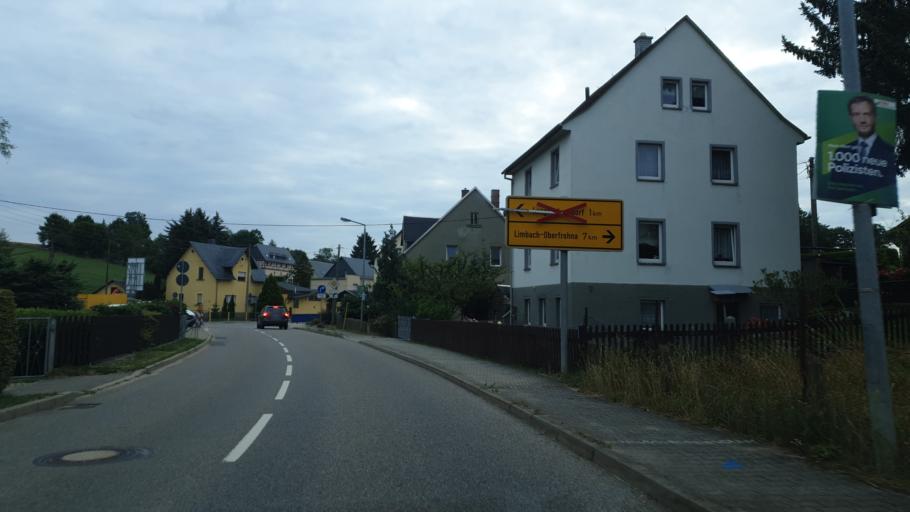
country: DE
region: Saxony
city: Hohenstein-Ernstthal
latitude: 50.8414
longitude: 12.6854
